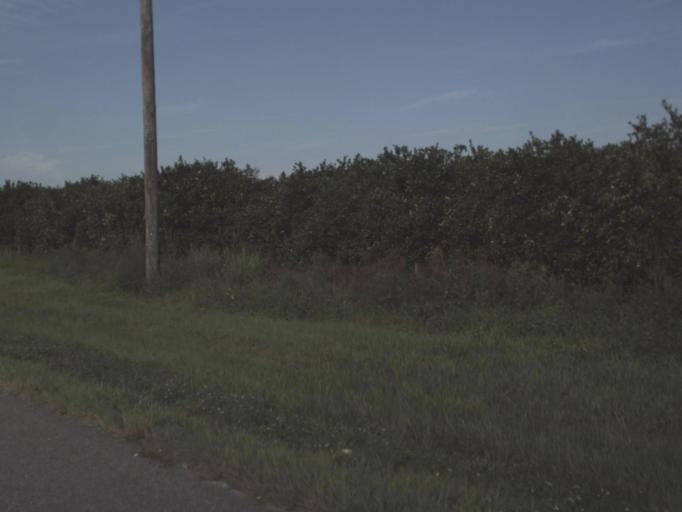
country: US
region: Florida
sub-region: Highlands County
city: Avon Park
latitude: 27.5642
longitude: -81.6412
